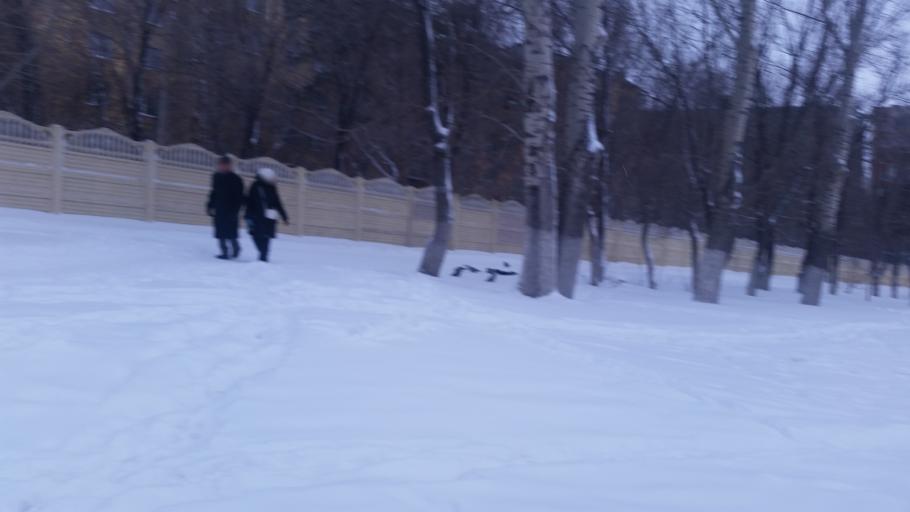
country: KZ
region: Qaraghandy
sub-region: Qaraghandy Qalasy
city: Karagandy
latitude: 49.7684
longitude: 73.1496
